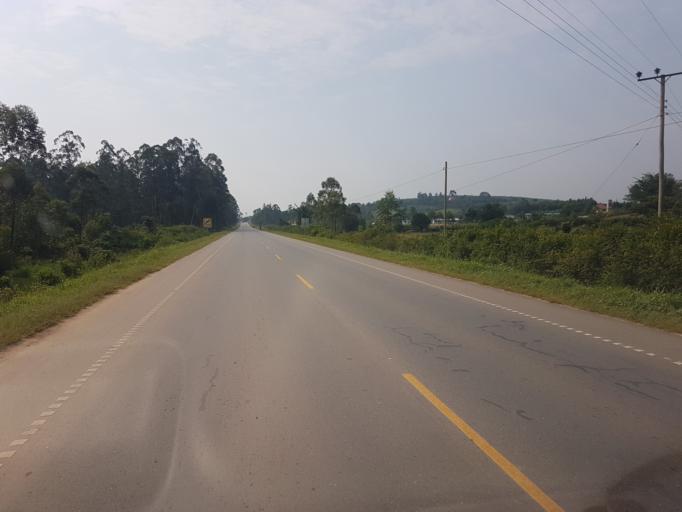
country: UG
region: Western Region
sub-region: Mbarara District
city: Bwizibwera
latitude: -0.6401
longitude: 30.5526
